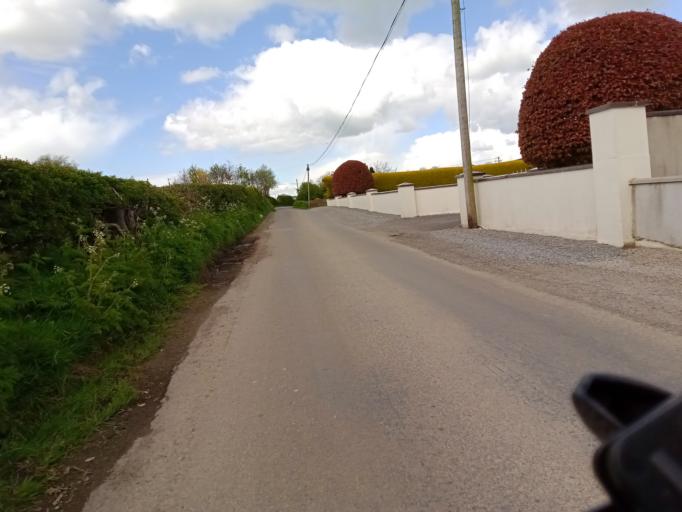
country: IE
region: Leinster
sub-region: Kilkenny
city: Thomastown
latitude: 52.5960
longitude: -7.1524
